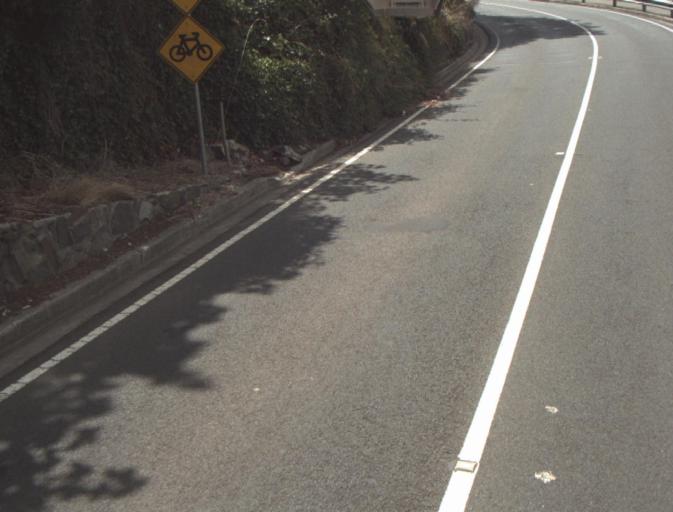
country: AU
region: Tasmania
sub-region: Launceston
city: Launceston
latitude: -41.4397
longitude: 147.1269
